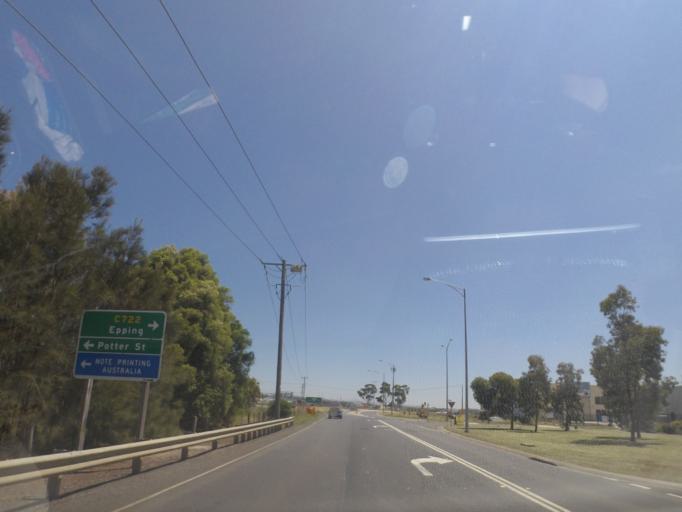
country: AU
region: Victoria
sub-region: Hume
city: Craigieburn
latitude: -37.6011
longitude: 144.9460
